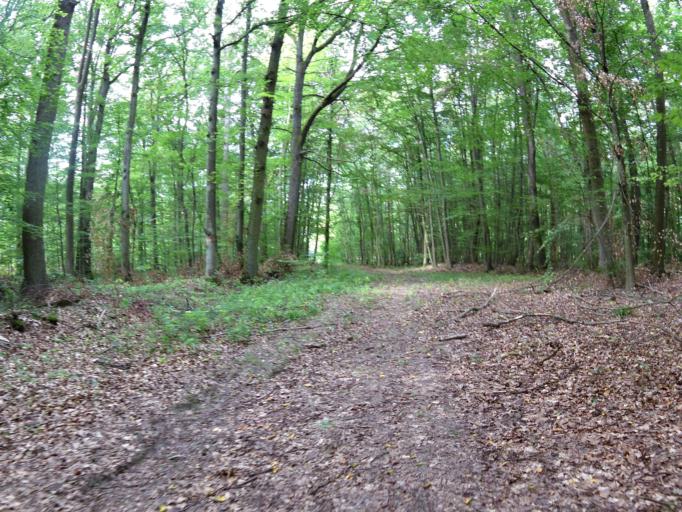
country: DE
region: Bavaria
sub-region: Regierungsbezirk Unterfranken
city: Waldbrunn
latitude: 49.7187
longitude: 9.8032
